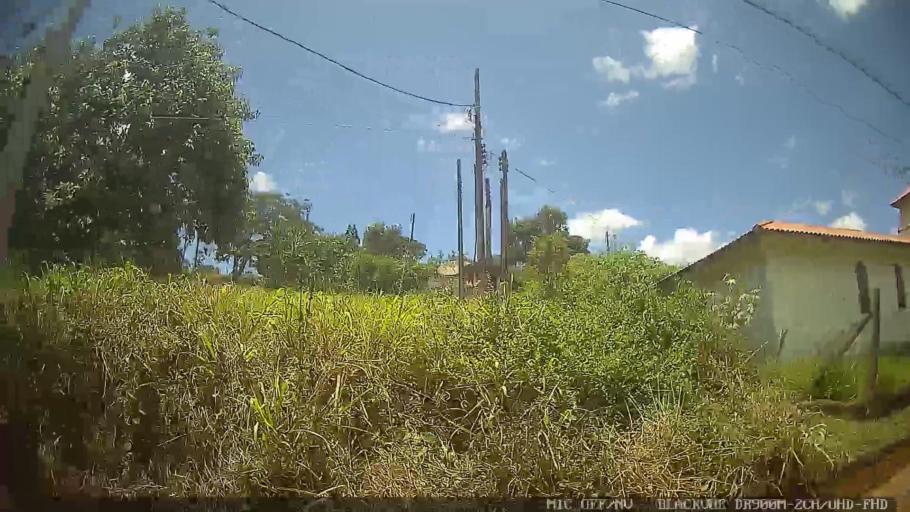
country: BR
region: Sao Paulo
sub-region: Piracaia
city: Piracaia
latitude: -23.0194
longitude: -46.4567
